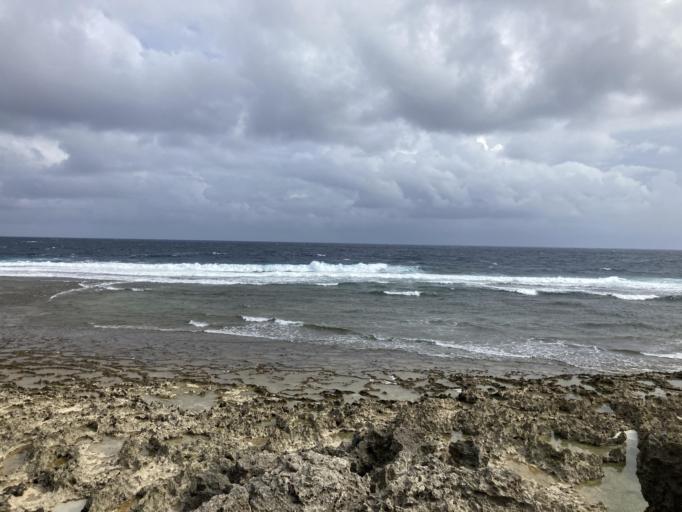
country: JP
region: Okinawa
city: Itoman
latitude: 26.0771
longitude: 127.6823
